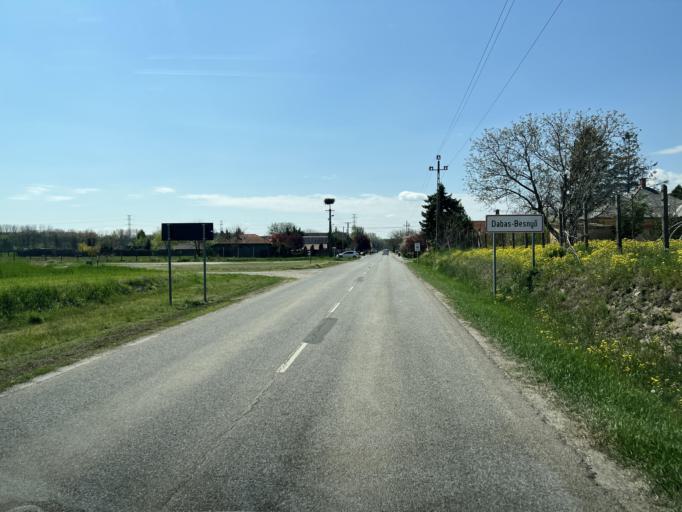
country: HU
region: Pest
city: Dabas
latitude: 47.2254
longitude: 19.2938
